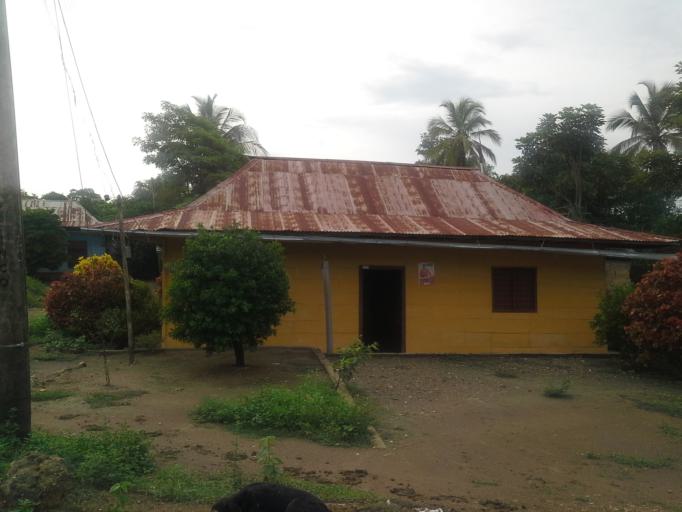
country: CO
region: Sucre
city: Coloso
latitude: 9.4613
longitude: -75.3682
